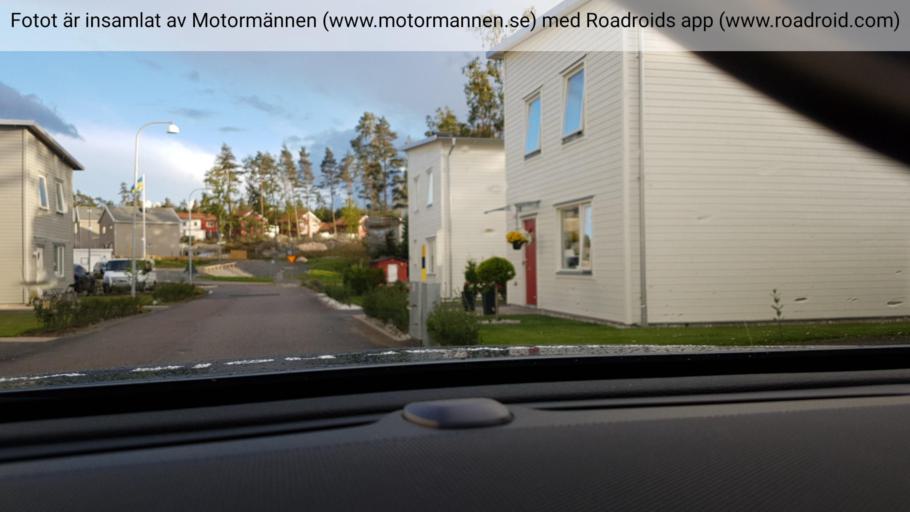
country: SE
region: Vaestra Goetaland
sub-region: Ale Kommun
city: Alvangen
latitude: 57.9502
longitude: 12.1252
